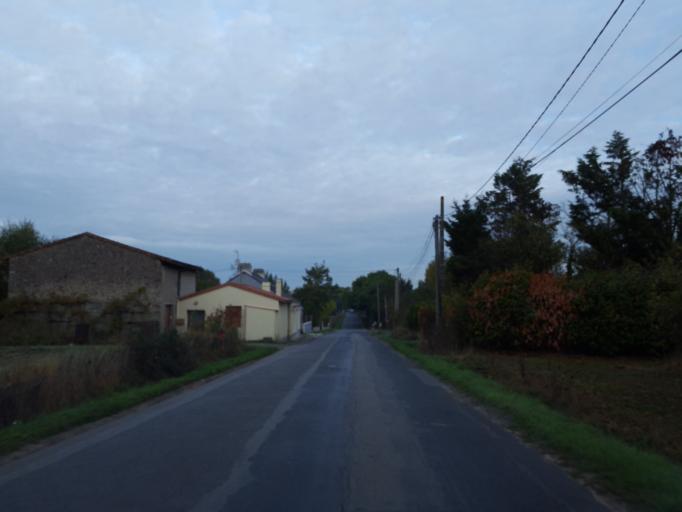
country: FR
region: Pays de la Loire
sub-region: Departement de la Loire-Atlantique
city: Saint-Julien-de-Concelles
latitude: 47.2489
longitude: -1.4032
